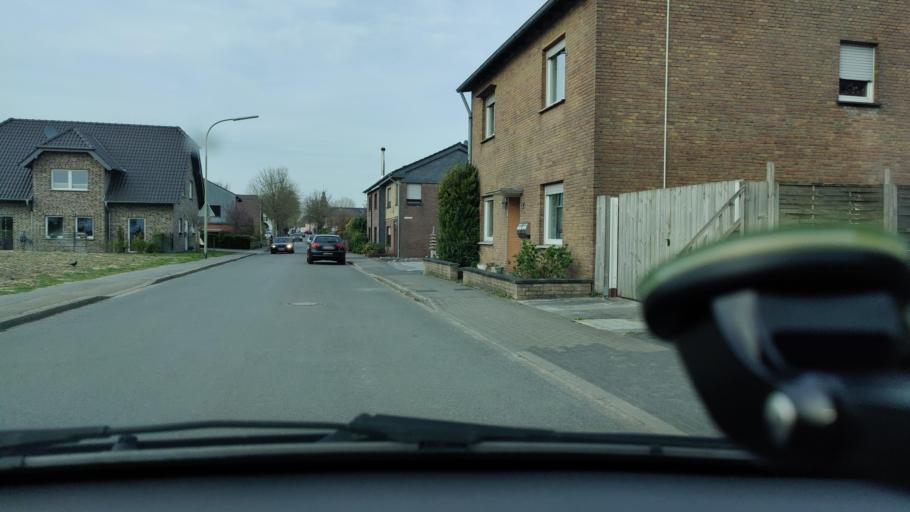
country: DE
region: North Rhine-Westphalia
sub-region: Regierungsbezirk Dusseldorf
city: Goch
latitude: 51.7035
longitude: 6.1612
